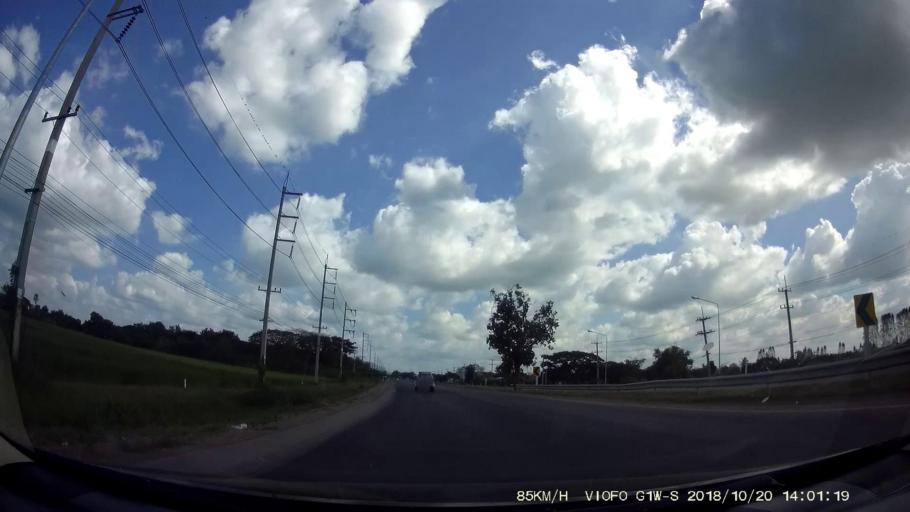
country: TH
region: Khon Kaen
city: Chum Phae
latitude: 16.5033
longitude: 102.1194
